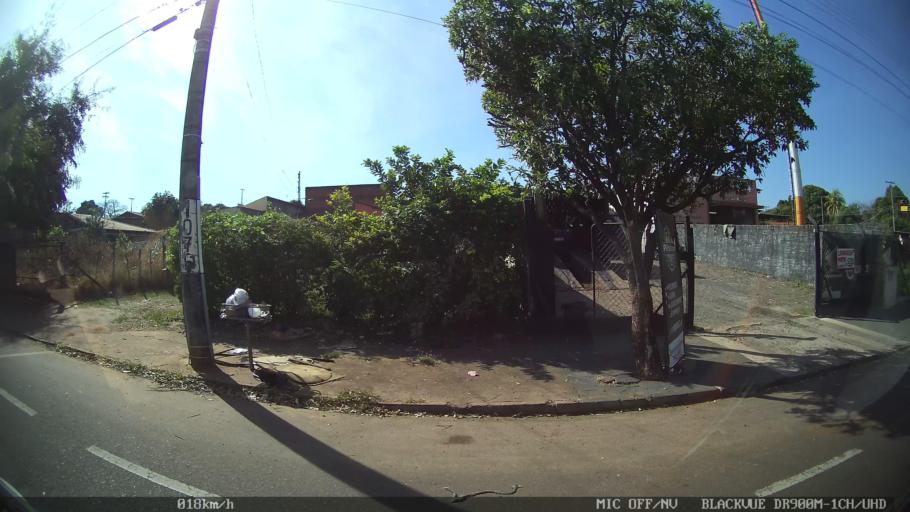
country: BR
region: Sao Paulo
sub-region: Sao Jose Do Rio Preto
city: Sao Jose do Rio Preto
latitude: -20.7913
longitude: -49.4068
